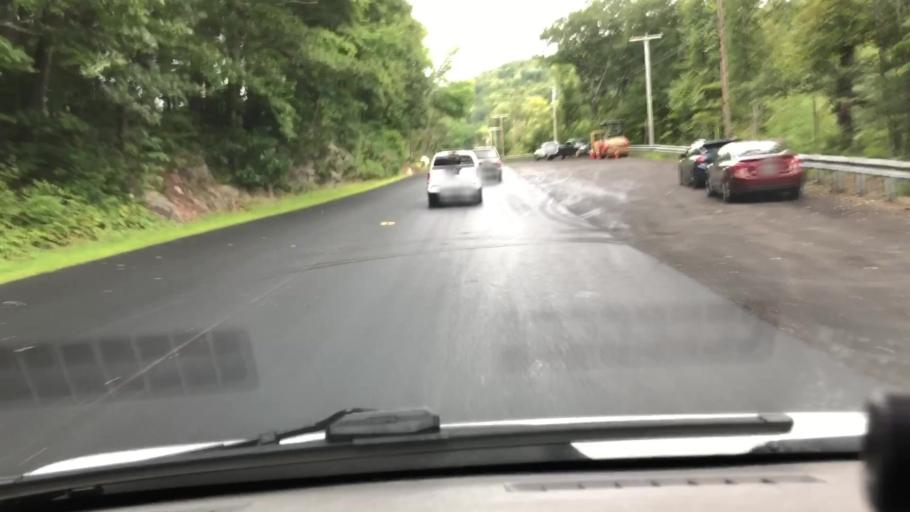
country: US
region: Massachusetts
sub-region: Franklin County
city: Buckland
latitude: 42.6191
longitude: -72.8204
